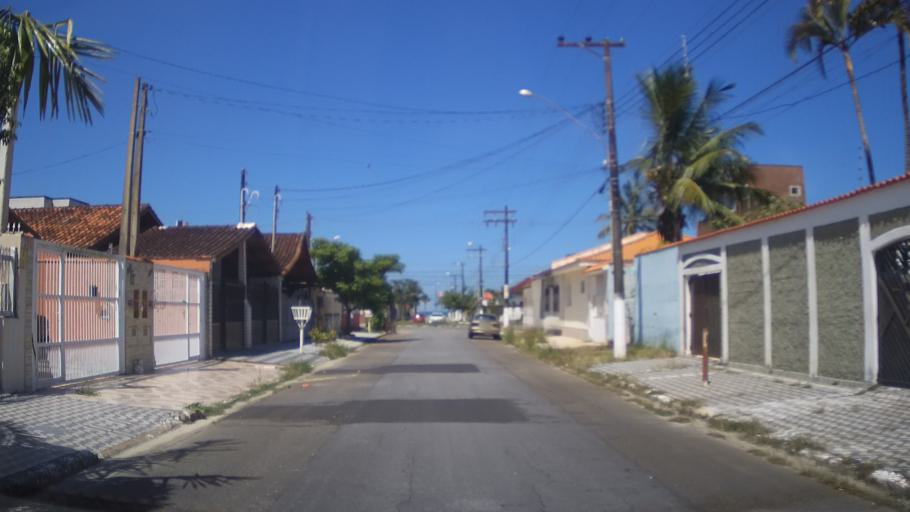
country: BR
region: Sao Paulo
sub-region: Mongagua
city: Mongagua
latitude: -24.0848
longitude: -46.6021
